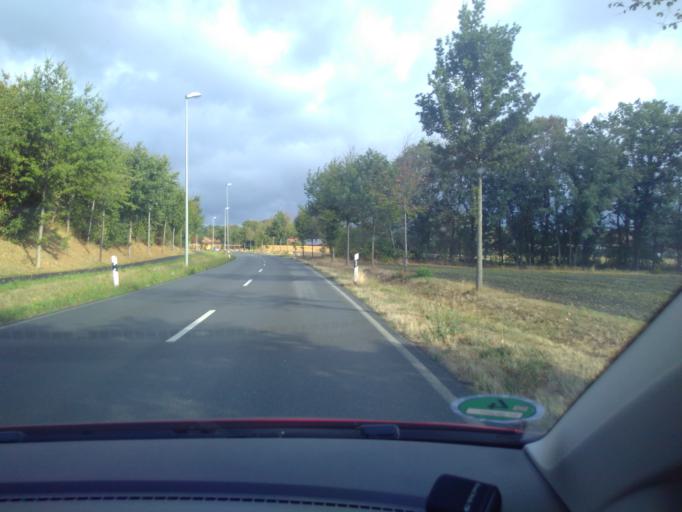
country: DE
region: North Rhine-Westphalia
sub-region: Regierungsbezirk Munster
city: Warendorf
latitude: 51.9591
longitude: 8.0100
